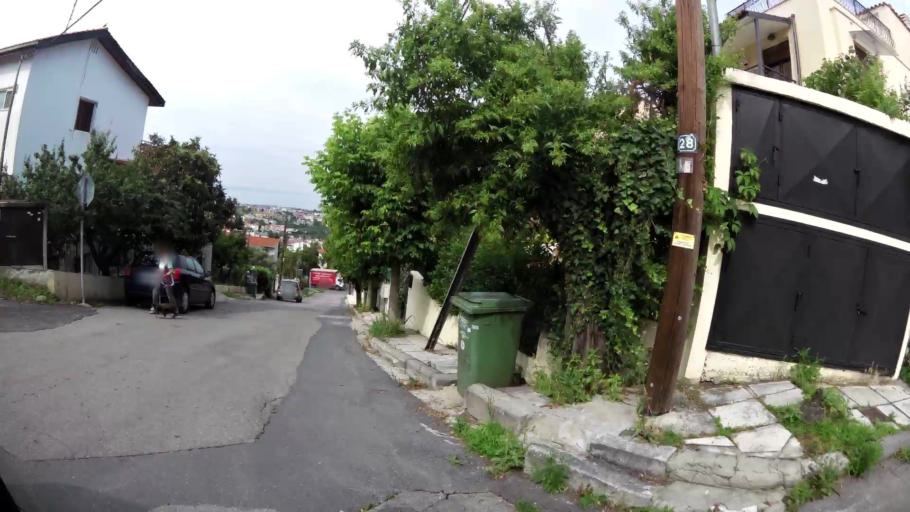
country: GR
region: Central Macedonia
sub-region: Nomos Thessalonikis
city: Panorama
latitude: 40.5886
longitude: 23.0204
